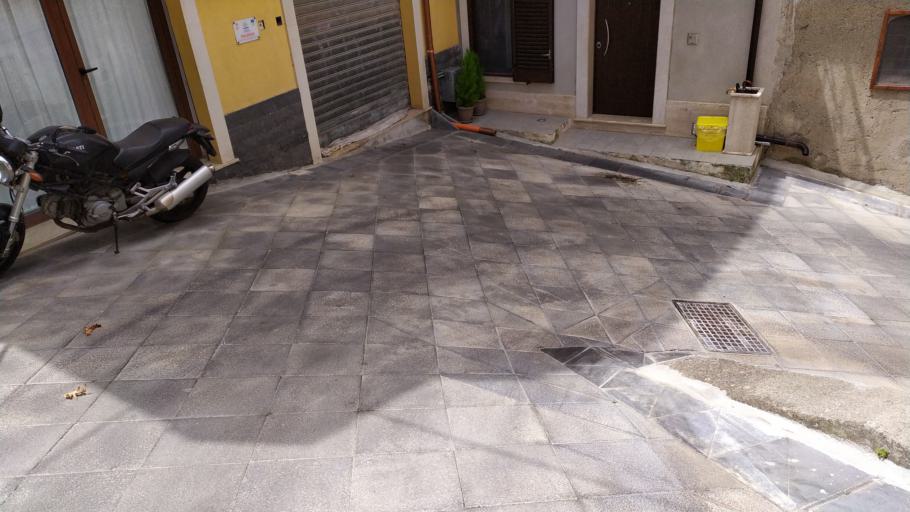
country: IT
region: Sicily
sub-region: Messina
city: San Pier Niceto
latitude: 38.1598
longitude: 15.3499
